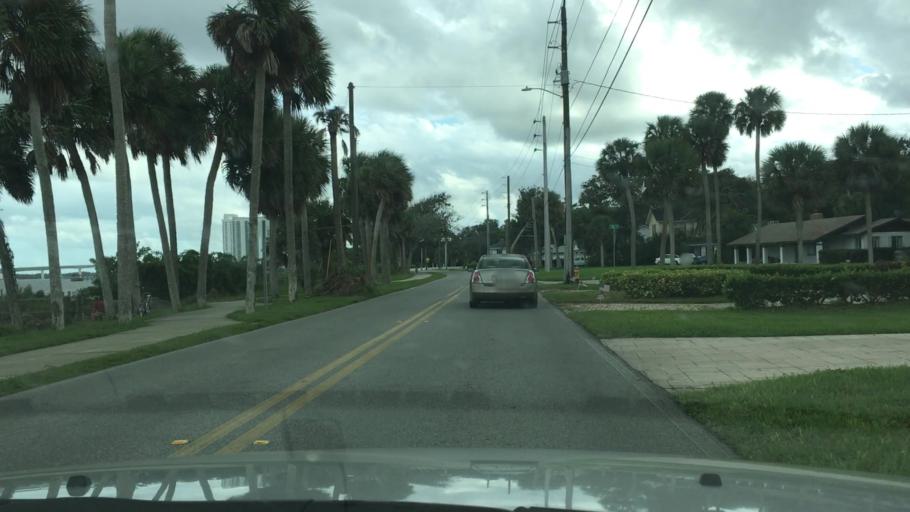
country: US
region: Florida
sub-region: Volusia County
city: Holly Hill
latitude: 29.2429
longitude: -81.0354
